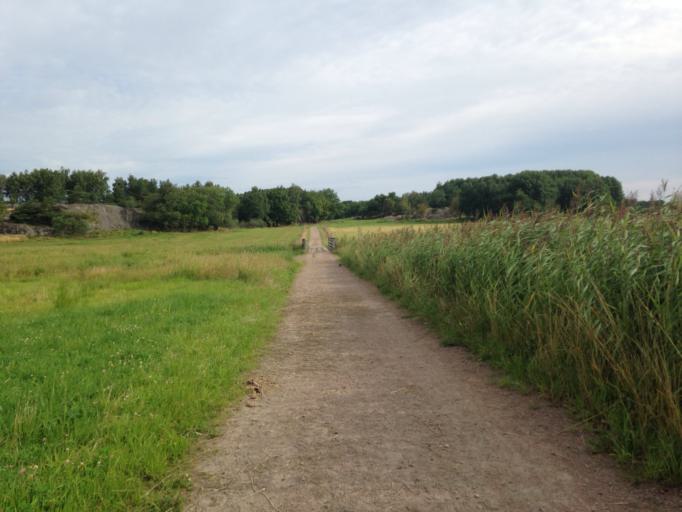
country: SE
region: Vaestra Goetaland
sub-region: Kungalvs Kommun
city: Kungalv
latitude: 57.8081
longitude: 11.8854
